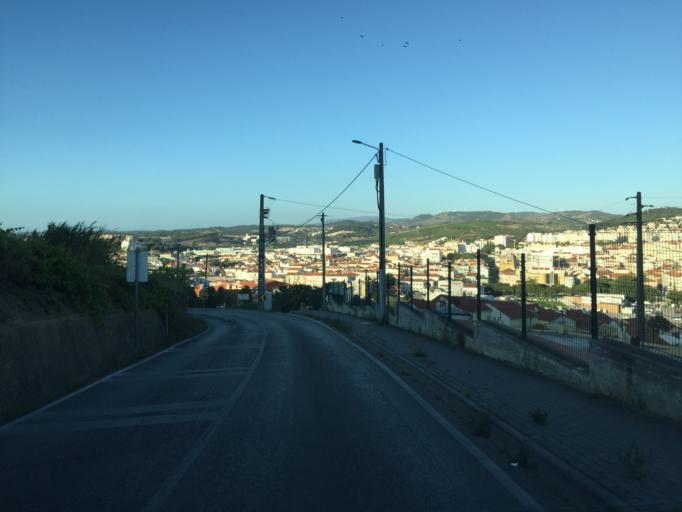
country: PT
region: Lisbon
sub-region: Torres Vedras
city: Torres Vedras
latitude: 39.0884
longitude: -9.2677
